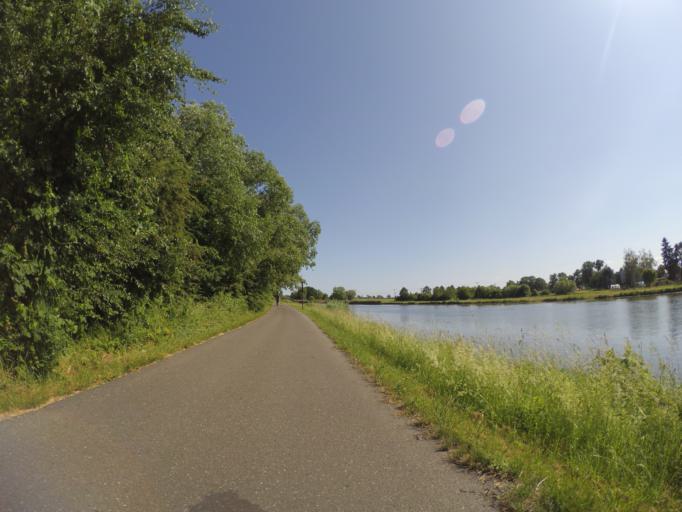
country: CZ
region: Central Bohemia
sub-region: Okres Nymburk
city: Nymburk
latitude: 50.1708
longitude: 15.0775
